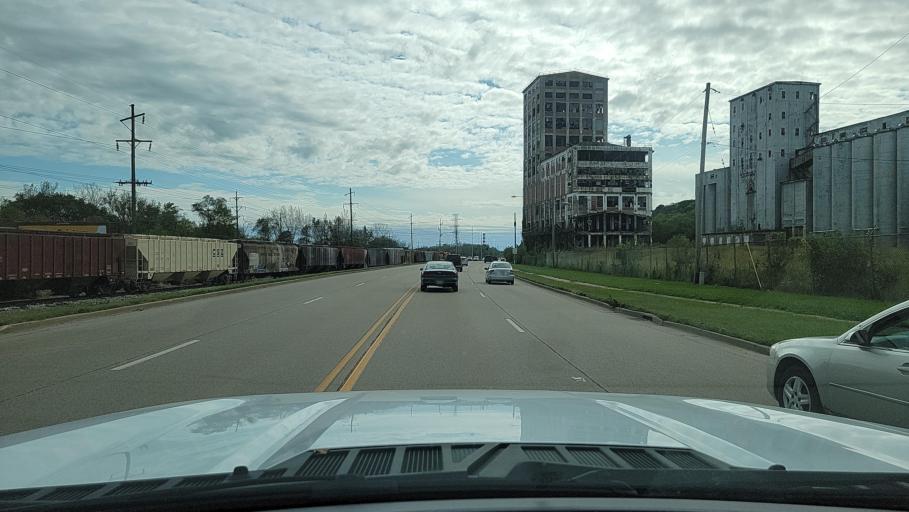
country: US
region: Illinois
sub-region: Peoria County
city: Bartonville
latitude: 40.6343
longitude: -89.6519
